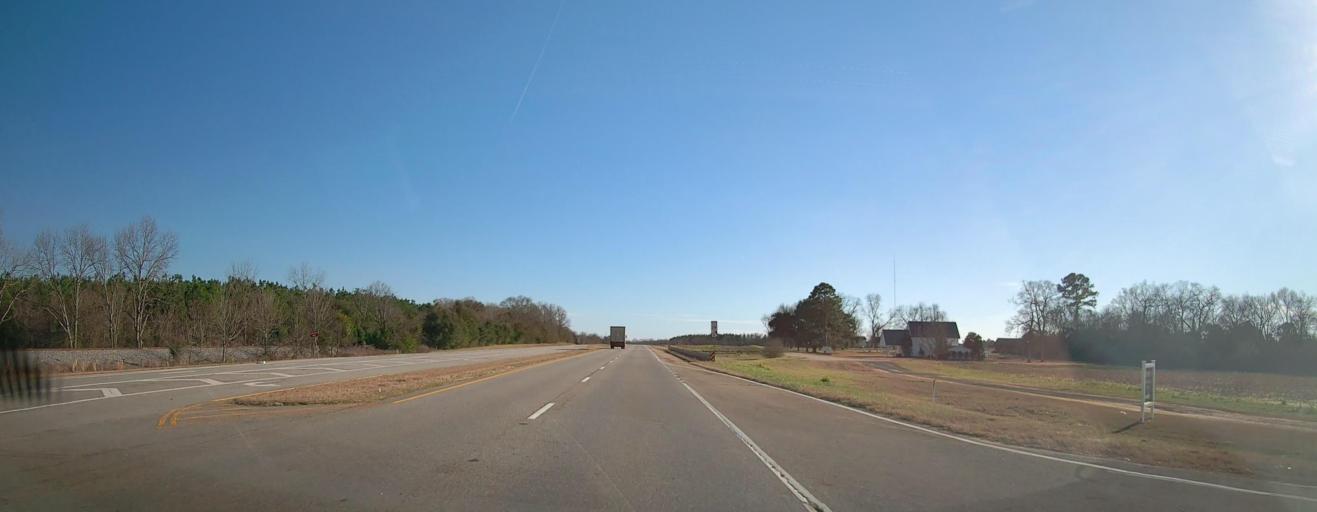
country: US
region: Georgia
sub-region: Sumter County
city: Americus
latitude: 31.9487
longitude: -84.2557
